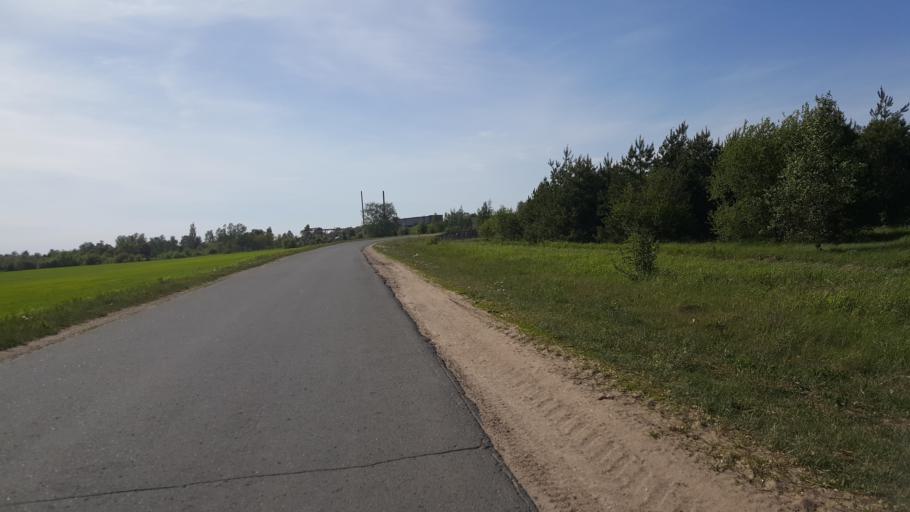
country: BY
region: Brest
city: Zhabinka
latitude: 52.3197
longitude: 23.9451
